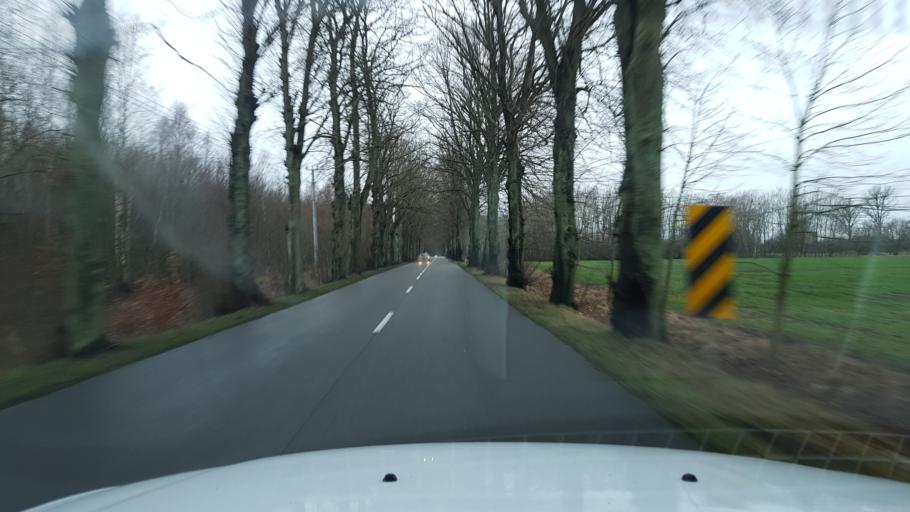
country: PL
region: West Pomeranian Voivodeship
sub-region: Powiat gryficki
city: Trzebiatow
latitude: 54.0583
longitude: 15.3271
